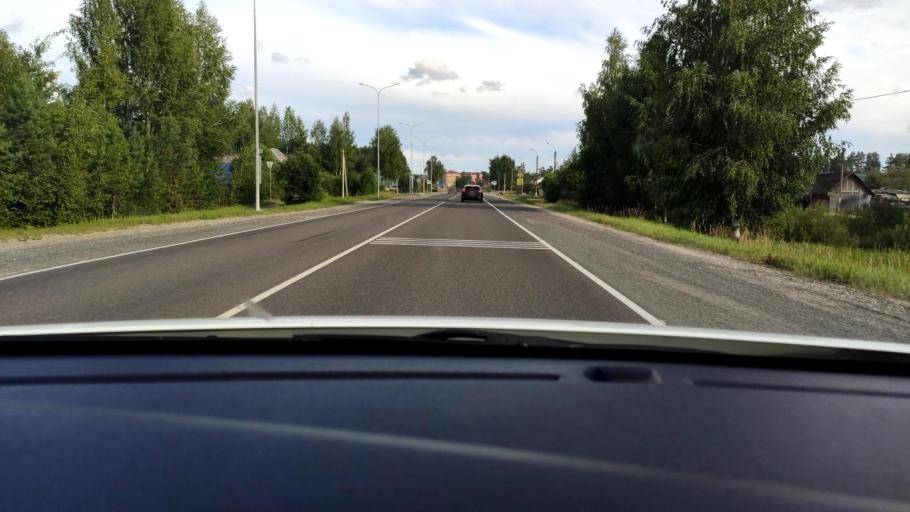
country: RU
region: Mariy-El
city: Suslonger
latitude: 56.3849
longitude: 48.1938
